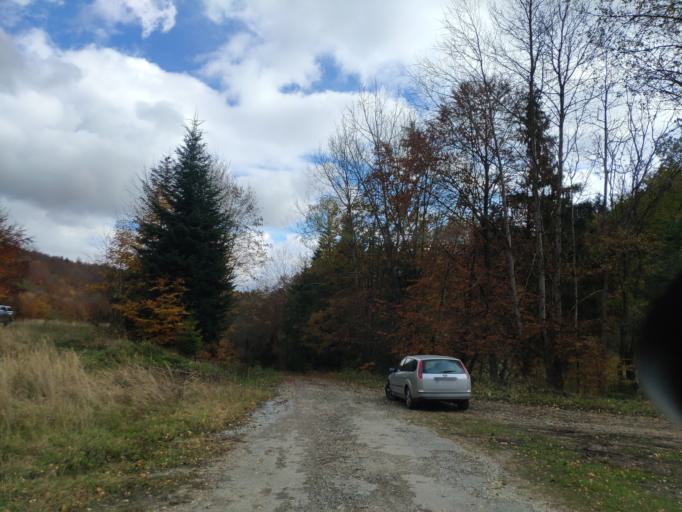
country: SK
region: Kosicky
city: Gelnica
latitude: 48.7609
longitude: 20.9809
